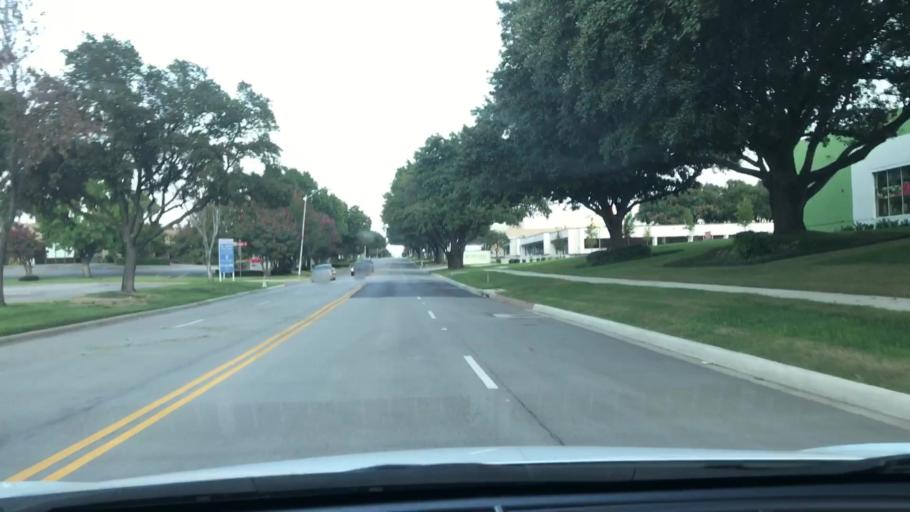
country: US
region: Texas
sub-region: Dallas County
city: Addison
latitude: 32.9330
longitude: -96.8376
